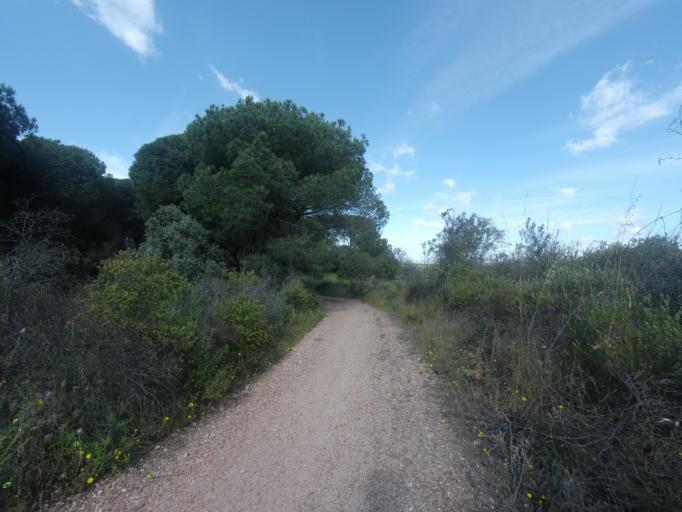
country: ES
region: Andalusia
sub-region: Provincia de Huelva
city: Aljaraque
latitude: 37.2345
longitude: -7.0418
